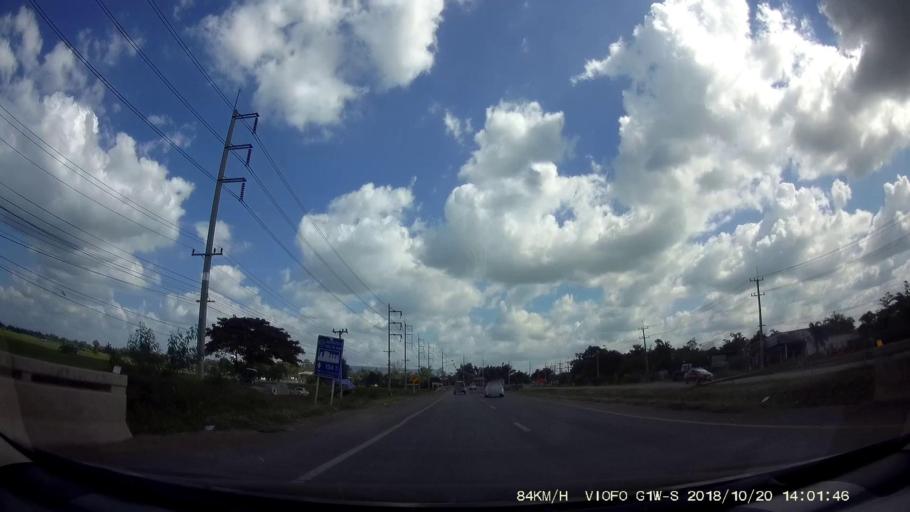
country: TH
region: Khon Kaen
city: Chum Phae
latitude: 16.4988
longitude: 102.1232
